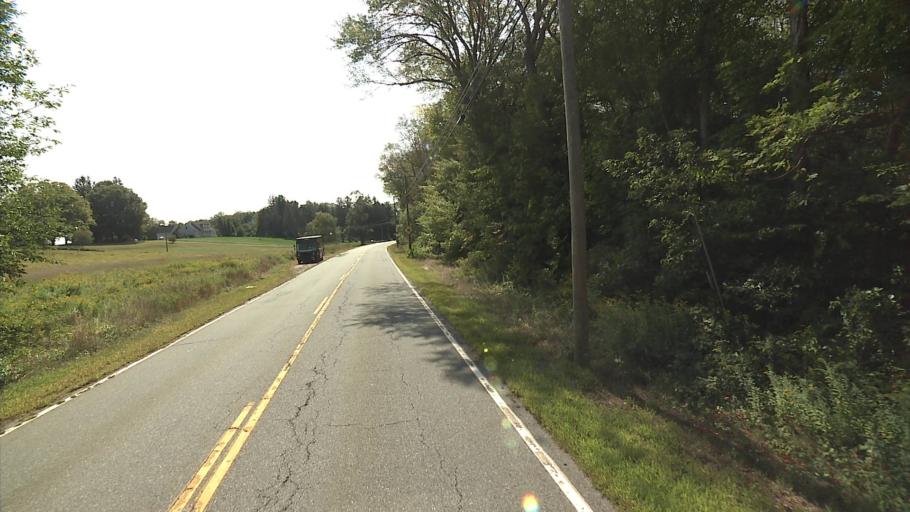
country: US
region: Connecticut
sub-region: Windham County
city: South Woodstock
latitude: 41.9619
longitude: -71.9837
